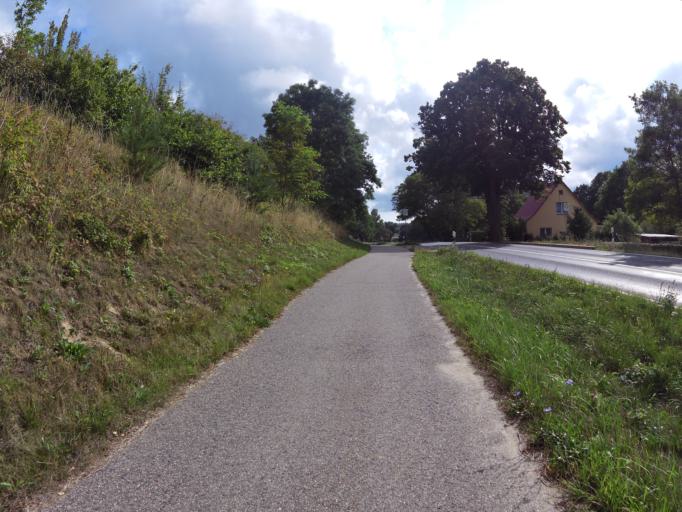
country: DE
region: Mecklenburg-Vorpommern
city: Seebad Bansin
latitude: 53.9621
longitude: 14.0625
